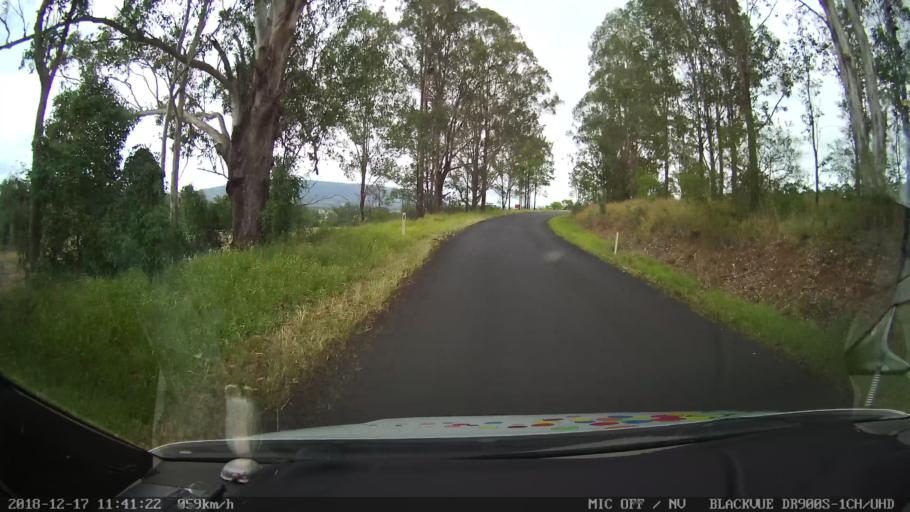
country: AU
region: New South Wales
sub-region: Kyogle
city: Kyogle
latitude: -28.6753
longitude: 152.5888
